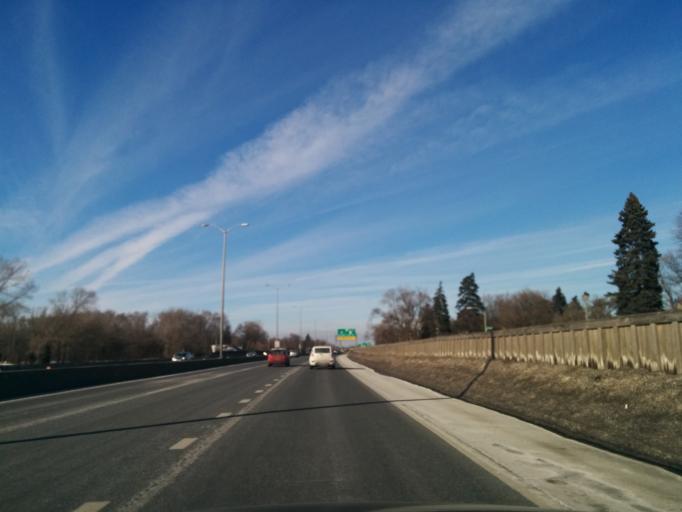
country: US
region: Illinois
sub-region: DuPage County
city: Elmhurst
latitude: 41.9124
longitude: -87.9659
